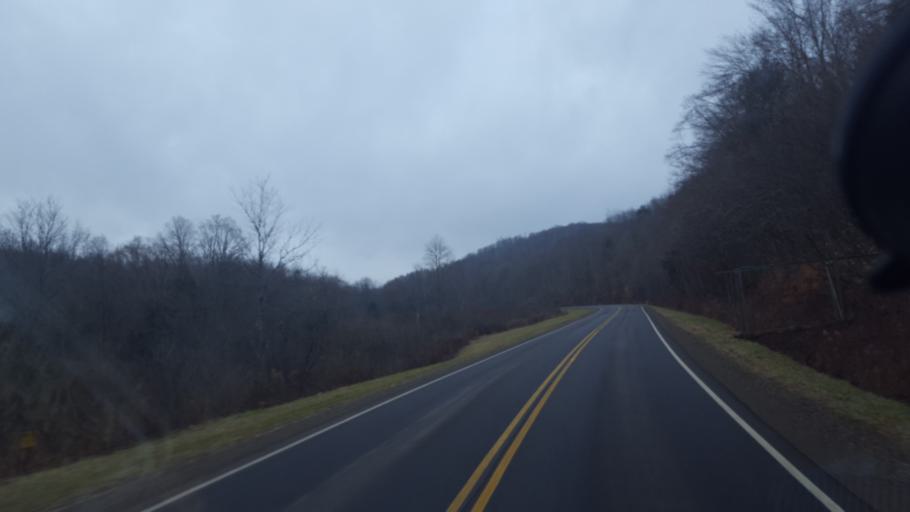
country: US
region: New York
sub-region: Allegany County
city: Andover
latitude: 42.0213
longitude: -77.7521
